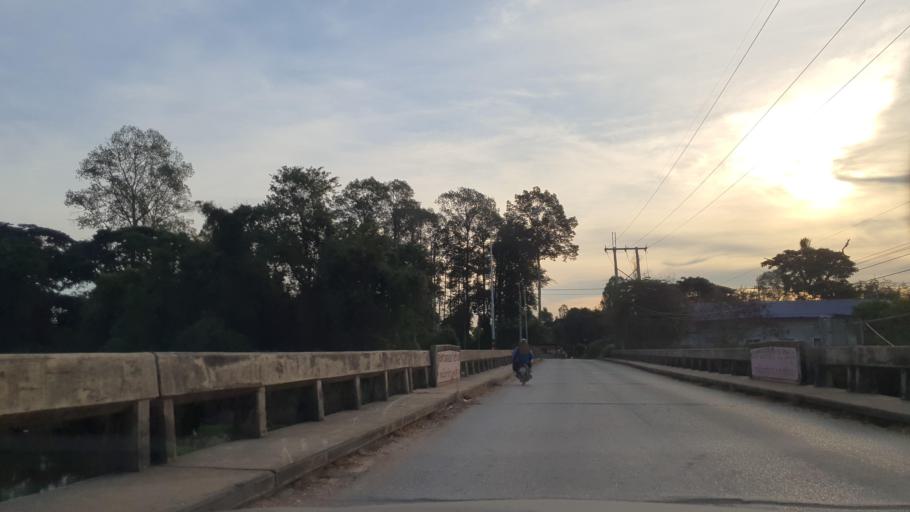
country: TH
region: Nakhon Sawan
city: Nakhon Sawan
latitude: 15.6631
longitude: 100.0586
